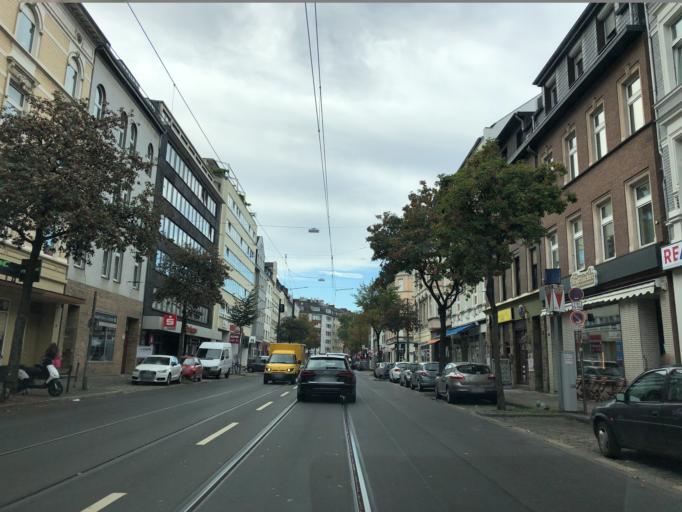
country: DE
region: North Rhine-Westphalia
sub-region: Regierungsbezirk Dusseldorf
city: Dusseldorf
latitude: 51.2108
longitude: 6.7695
